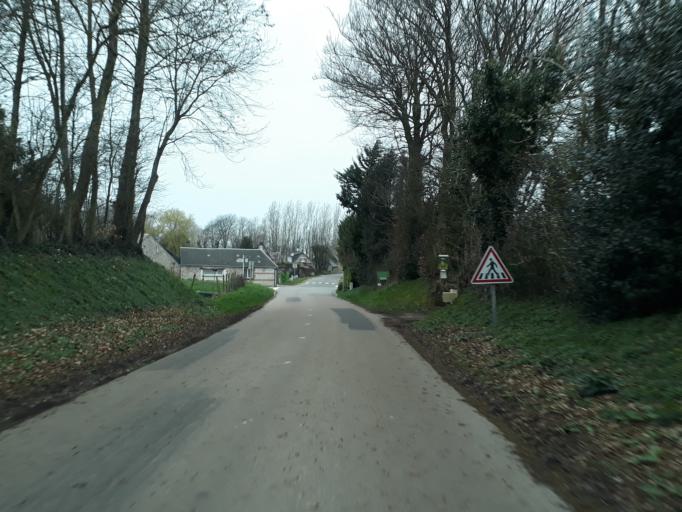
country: FR
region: Haute-Normandie
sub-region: Departement de la Seine-Maritime
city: Les Loges
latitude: 49.7214
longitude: 0.2811
